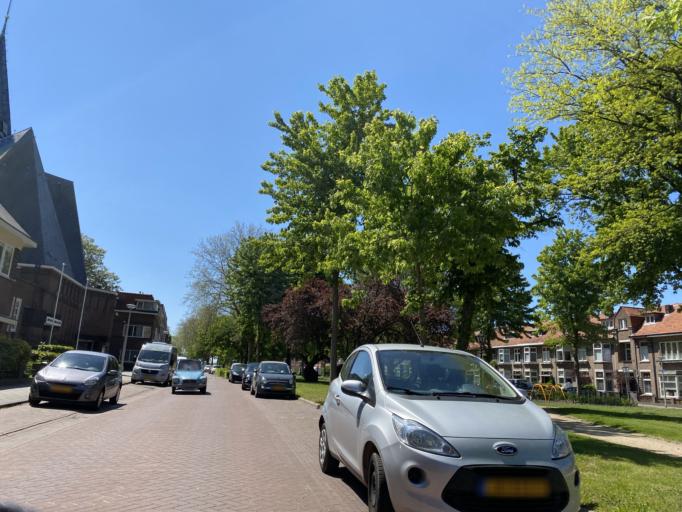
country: NL
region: North Brabant
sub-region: Gemeente Bergen op Zoom
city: Bergen op Zoom
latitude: 51.4991
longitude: 4.2867
